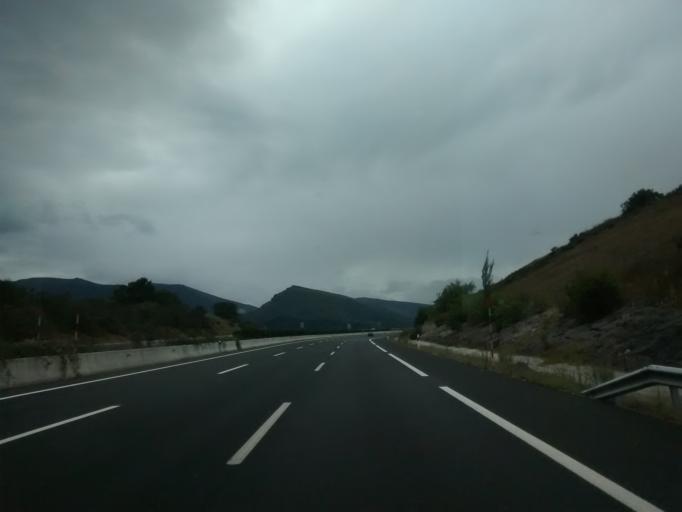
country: ES
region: Cantabria
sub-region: Provincia de Cantabria
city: Molledo
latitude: 43.1451
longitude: -4.0560
